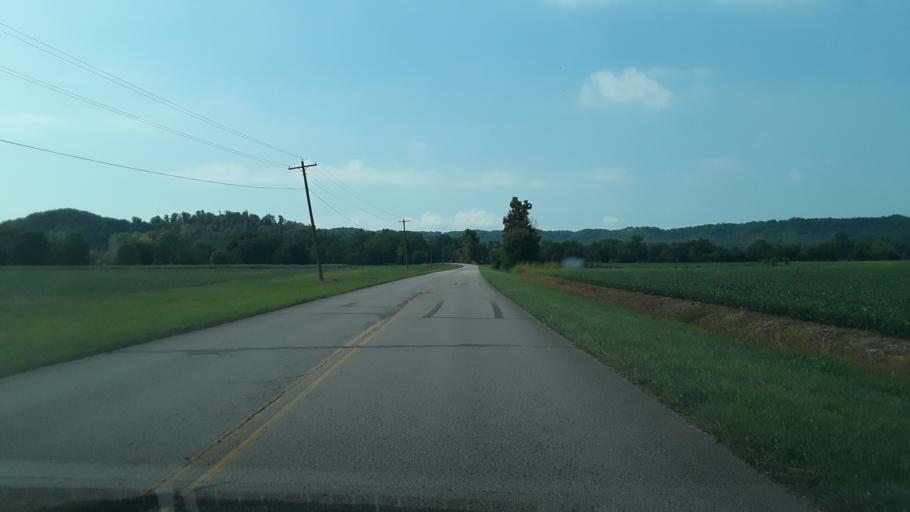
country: US
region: Indiana
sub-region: Clark County
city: Sellersburg
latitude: 38.4536
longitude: -85.8654
